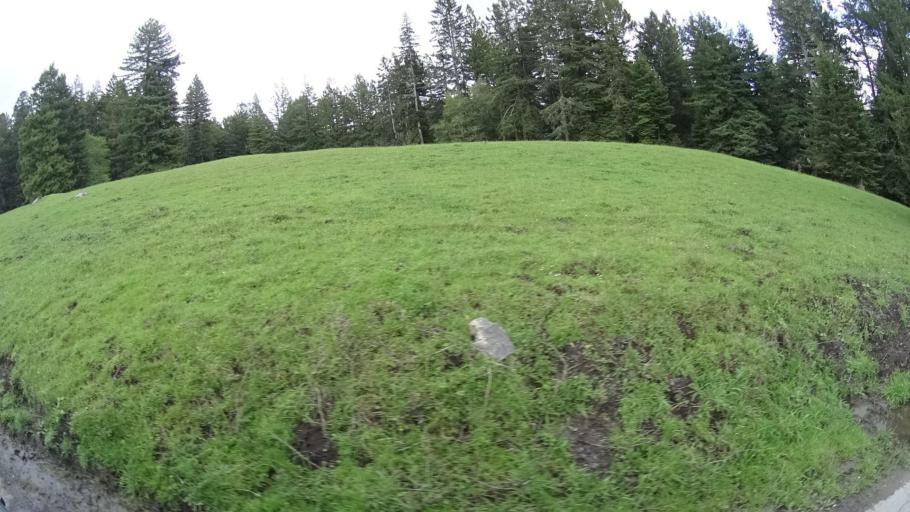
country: US
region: California
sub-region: Humboldt County
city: Blue Lake
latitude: 40.9085
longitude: -123.9676
